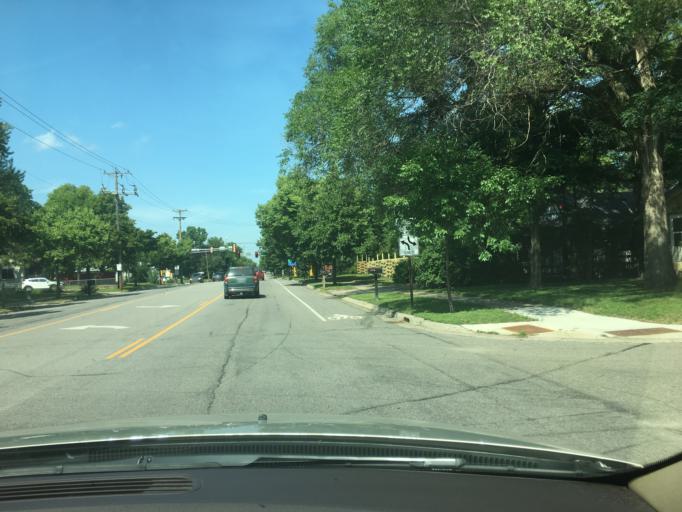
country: US
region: Minnesota
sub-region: Stearns County
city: Saint Cloud
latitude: 45.5418
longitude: -94.1612
